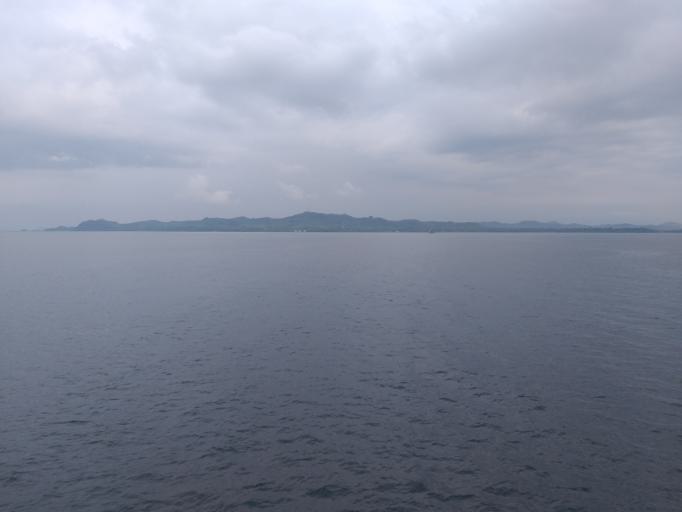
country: TH
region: Trat
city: Laem Ngop
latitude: 12.1564
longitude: 102.2890
